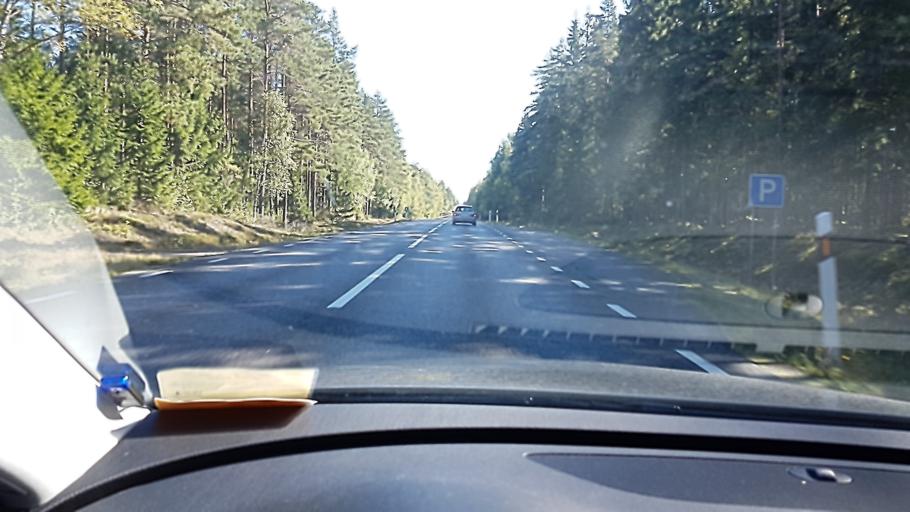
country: SE
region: Kronoberg
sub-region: Lessebo Kommun
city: Lessebo
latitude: 56.7313
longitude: 15.3969
